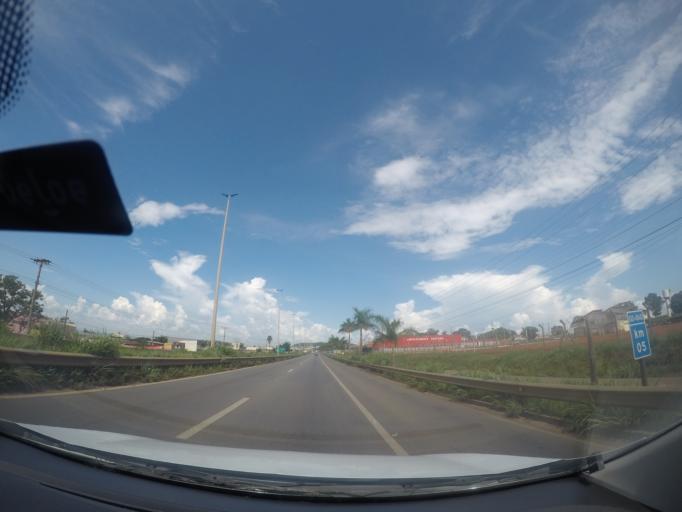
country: BR
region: Goias
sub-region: Trindade
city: Trindade
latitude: -16.6579
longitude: -49.3741
